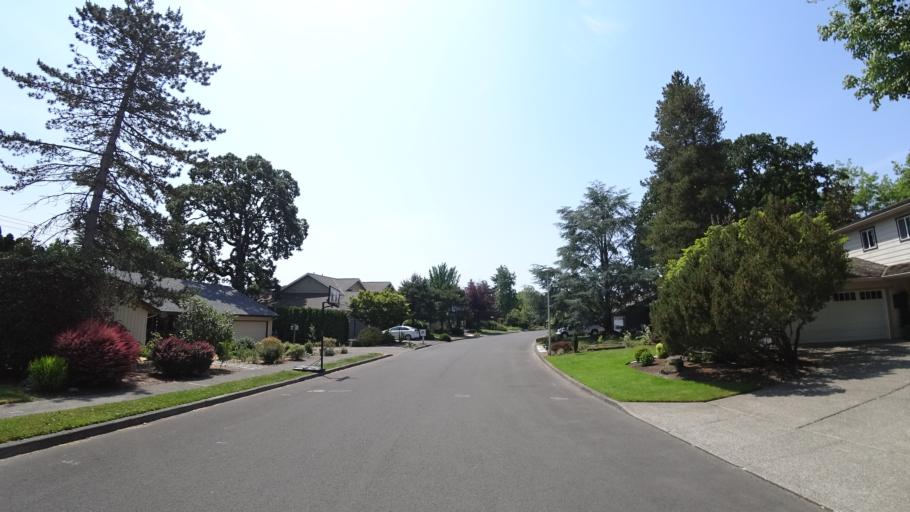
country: US
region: Oregon
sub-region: Washington County
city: Oak Hills
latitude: 45.5404
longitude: -122.8281
